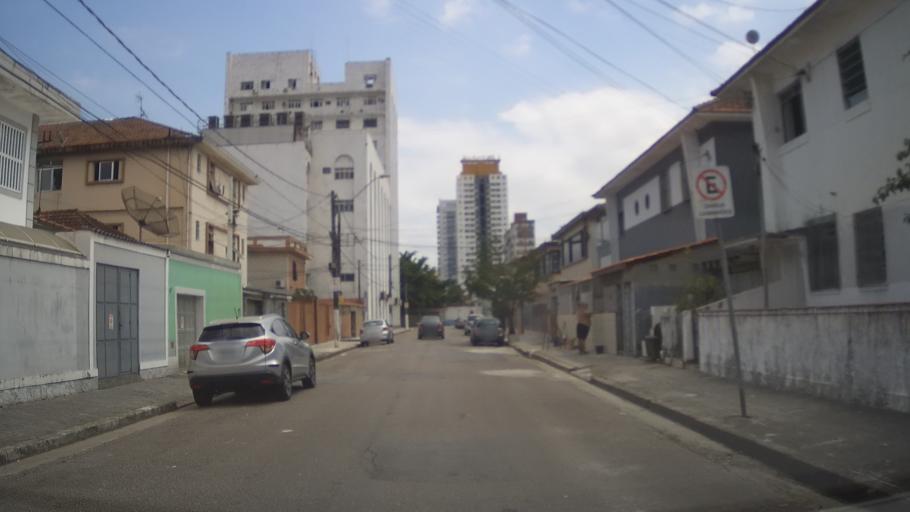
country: BR
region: Sao Paulo
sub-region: Santos
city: Santos
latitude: -23.9571
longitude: -46.3176
